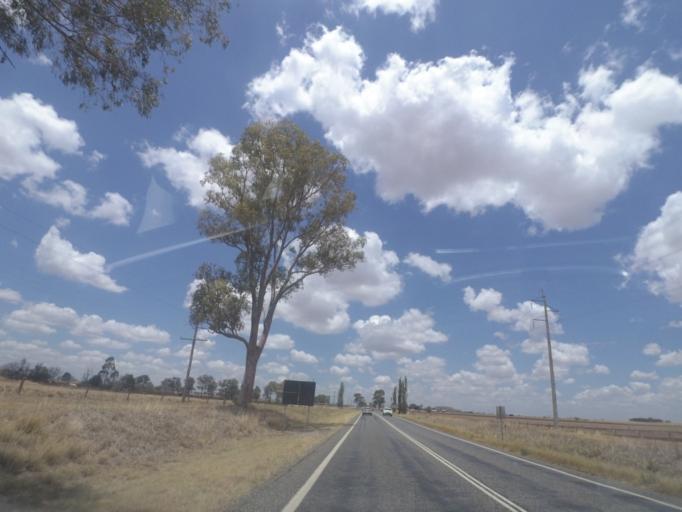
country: AU
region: Queensland
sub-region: Toowoomba
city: Top Camp
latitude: -27.9247
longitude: 151.9840
